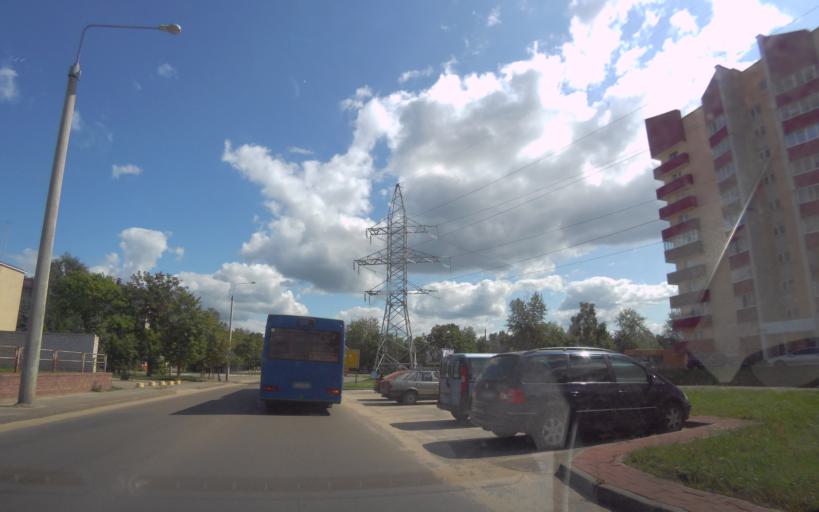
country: BY
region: Minsk
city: Horad Barysaw
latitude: 54.2160
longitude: 28.4774
